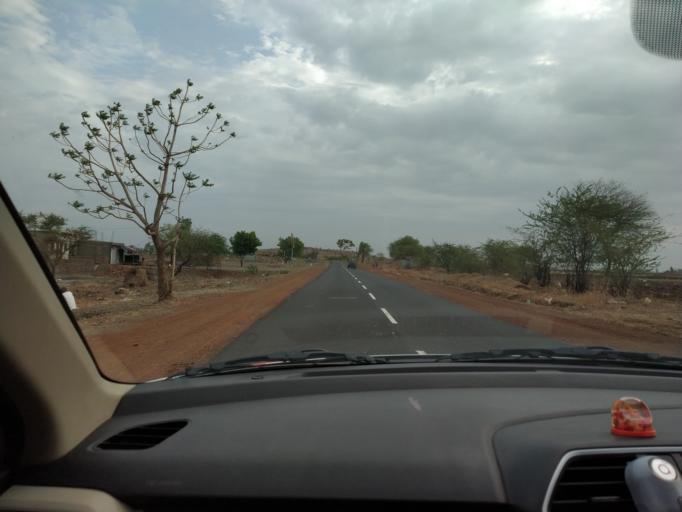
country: IN
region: Madhya Pradesh
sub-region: Shajapur
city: Agar
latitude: 23.6426
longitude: 75.9773
